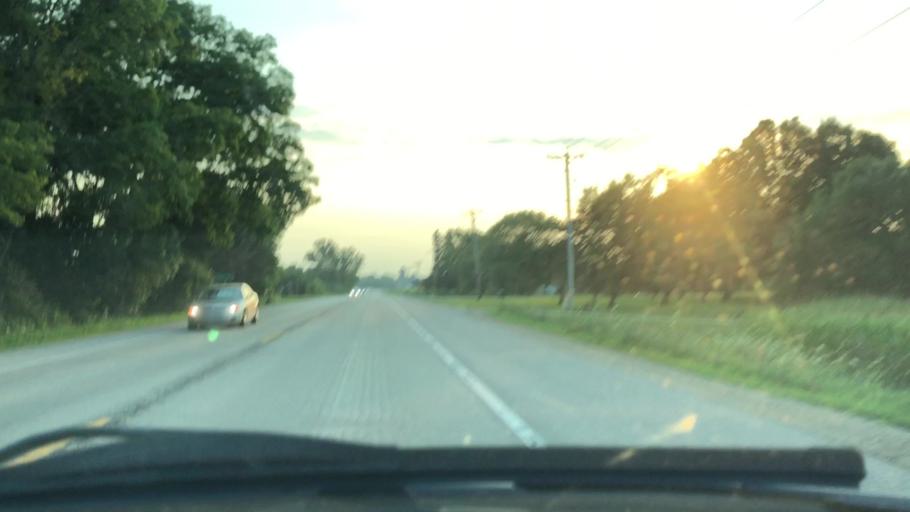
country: US
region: Wisconsin
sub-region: Dane County
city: Mazomanie
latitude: 43.1620
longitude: -89.8372
